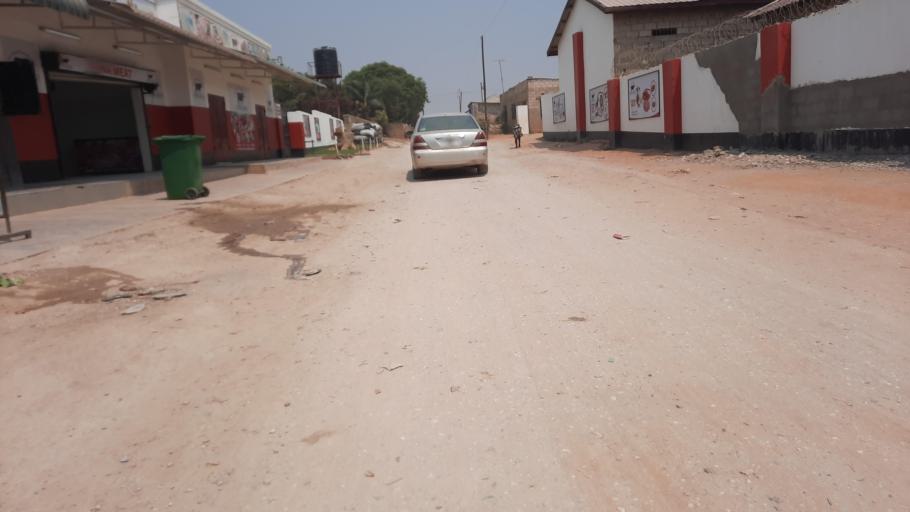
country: ZM
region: Lusaka
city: Lusaka
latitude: -15.4084
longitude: 28.3714
